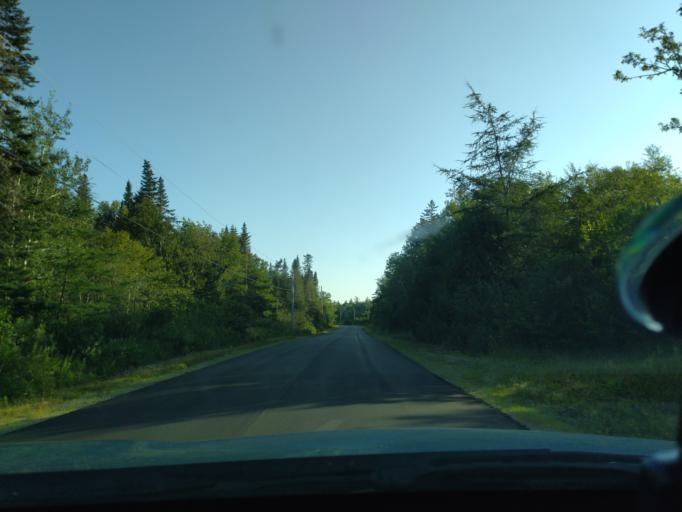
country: US
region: Maine
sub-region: Washington County
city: East Machias
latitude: 44.6960
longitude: -67.1614
